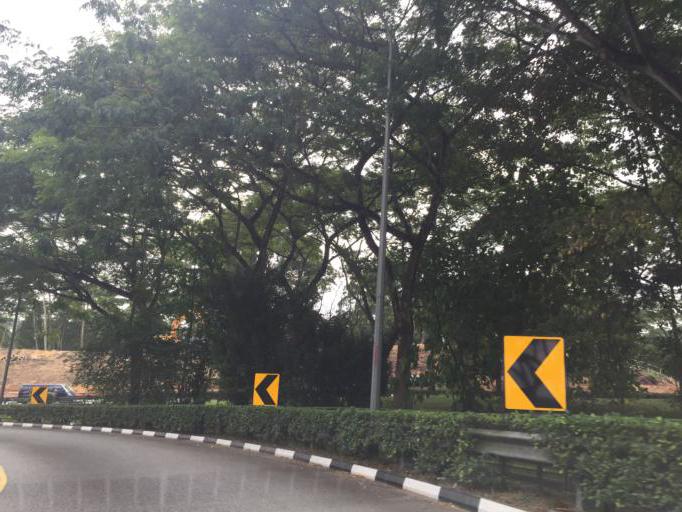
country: SG
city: Singapore
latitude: 1.3333
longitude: 103.8166
